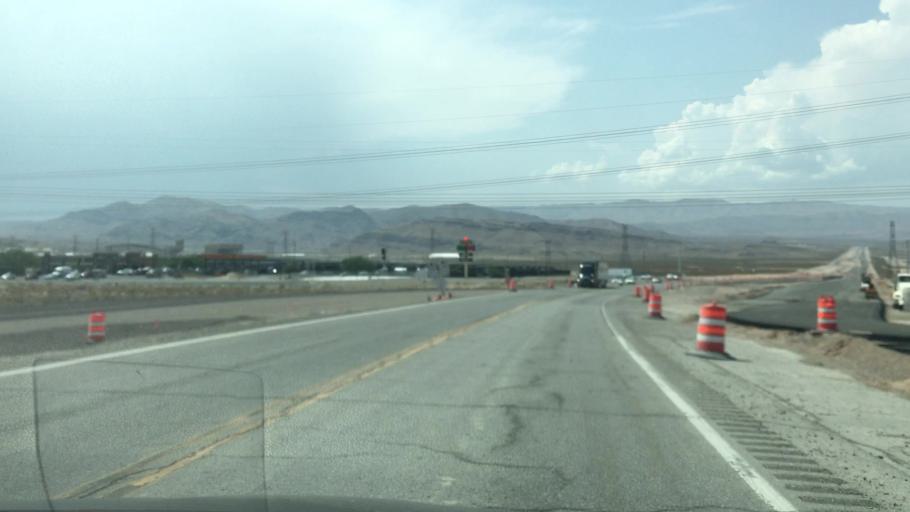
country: US
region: Nevada
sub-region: Clark County
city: Nellis Air Force Base
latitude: 36.3816
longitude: -114.8931
